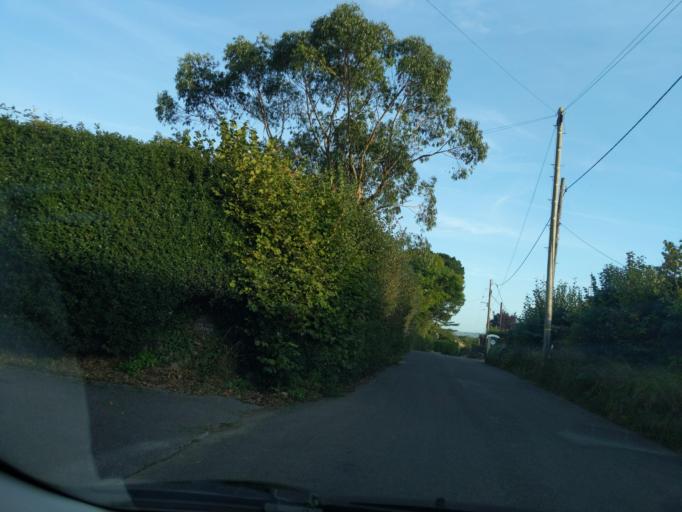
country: GB
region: England
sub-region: Devon
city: Bovey Tracey
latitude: 50.5929
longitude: -3.6642
